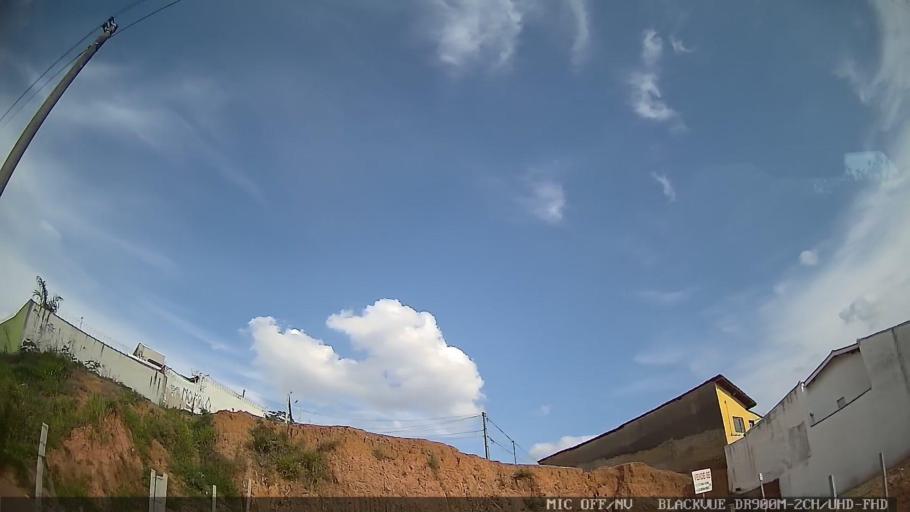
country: BR
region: Sao Paulo
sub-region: Braganca Paulista
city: Braganca Paulista
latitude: -22.9258
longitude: -46.5367
